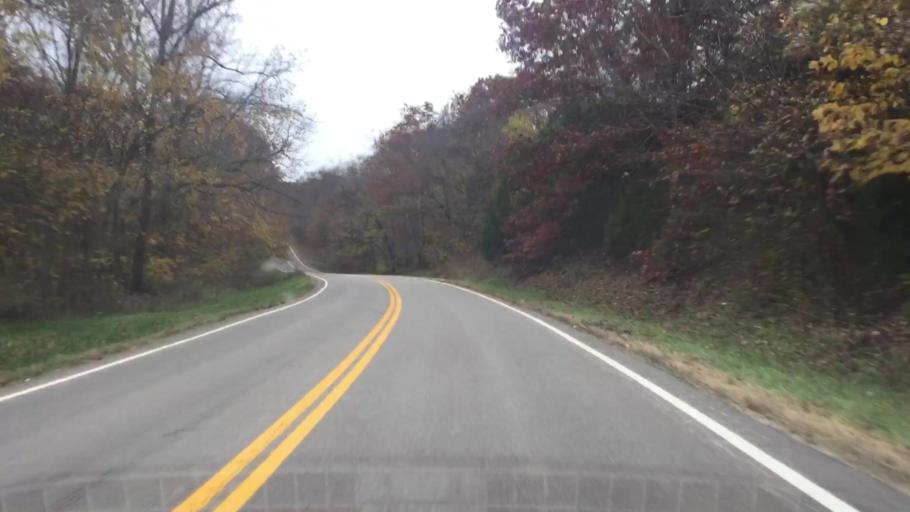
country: US
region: Missouri
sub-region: Gasconade County
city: Hermann
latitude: 38.7226
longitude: -91.6937
